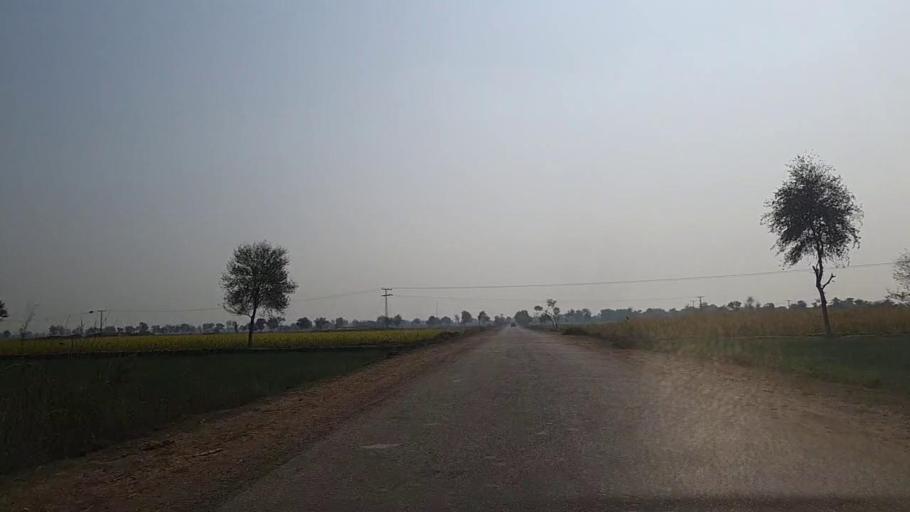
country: PK
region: Sindh
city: Jam Sahib
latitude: 26.3474
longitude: 68.5344
